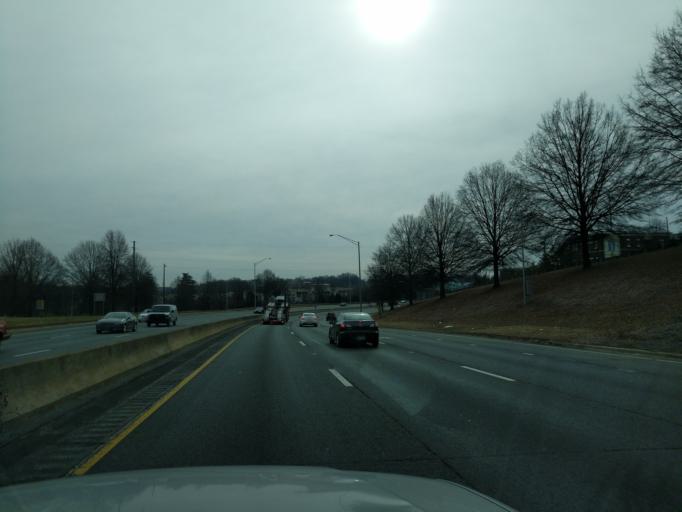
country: US
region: North Carolina
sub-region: Mecklenburg County
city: Charlotte
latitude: 35.2285
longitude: -80.8298
